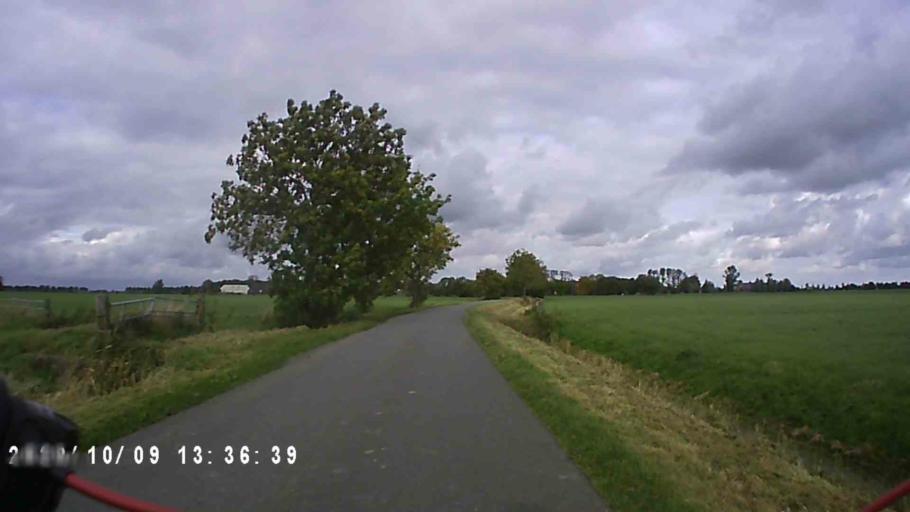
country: NL
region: Groningen
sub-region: Gemeente Zuidhorn
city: Aduard
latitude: 53.3000
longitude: 6.4681
